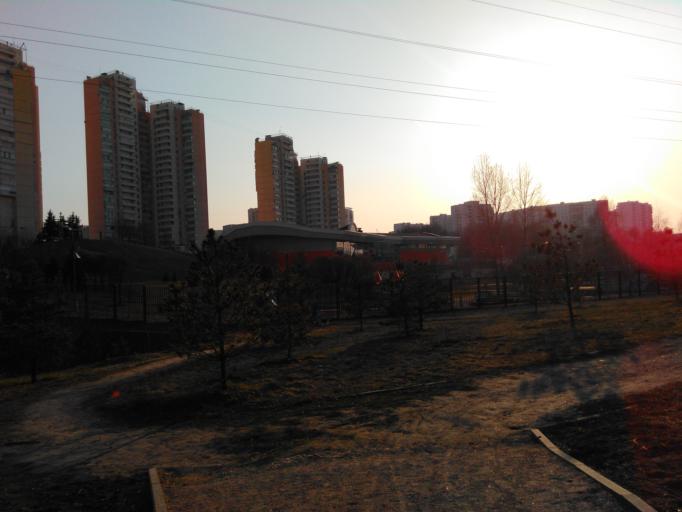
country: RU
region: Moscow
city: Nikol'skoye
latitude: 55.6870
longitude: 37.4944
